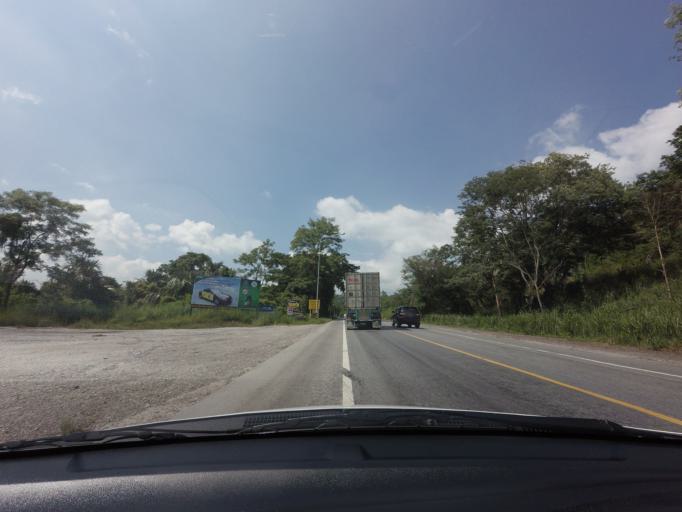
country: TH
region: Nakhon Ratchasima
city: Wang Nam Khiao
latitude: 14.2973
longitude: 101.8803
